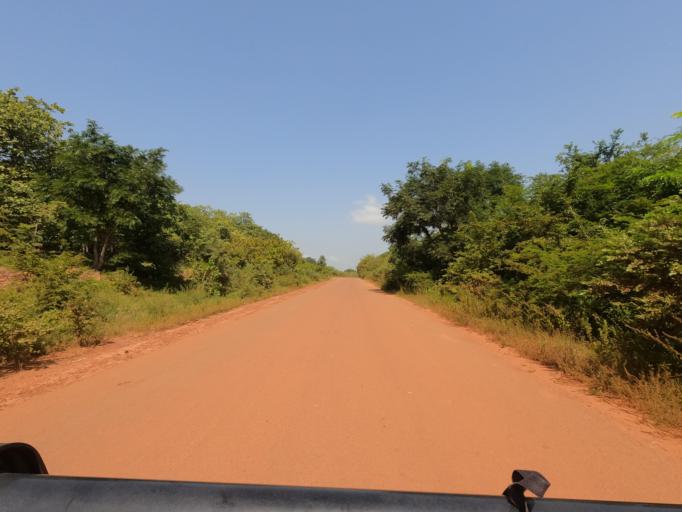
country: GW
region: Cacheu
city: Canchungo
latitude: 12.2671
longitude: -15.7870
